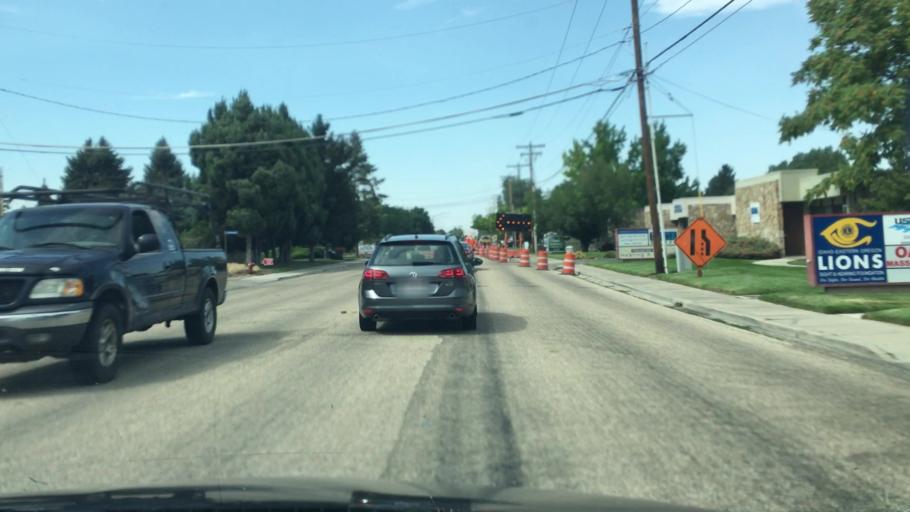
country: US
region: Idaho
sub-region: Ada County
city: Garden City
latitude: 43.6141
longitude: -116.2742
